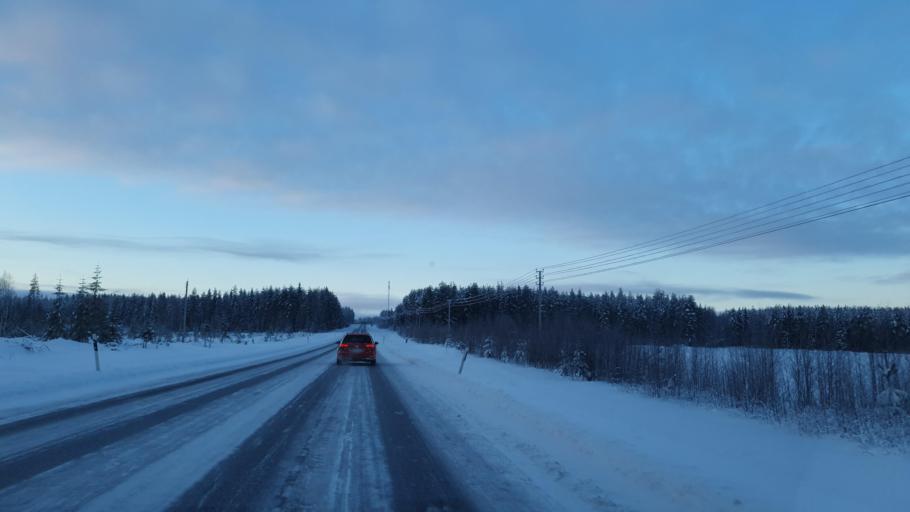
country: FI
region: Kainuu
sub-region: Kajaani
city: Paltamo
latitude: 64.4193
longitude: 27.7065
